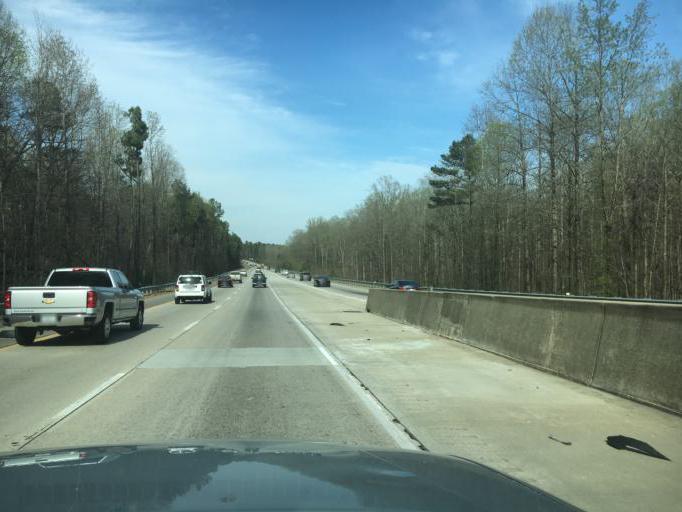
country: US
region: Georgia
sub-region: Hall County
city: Oakwood
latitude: 34.2323
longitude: -83.8498
